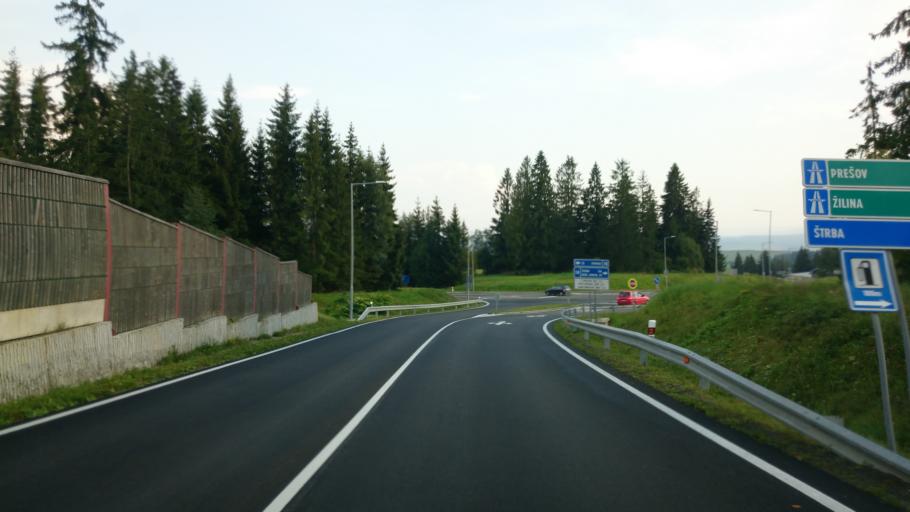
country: SK
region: Presovsky
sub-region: Okres Poprad
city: Strba
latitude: 49.0839
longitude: 20.0715
